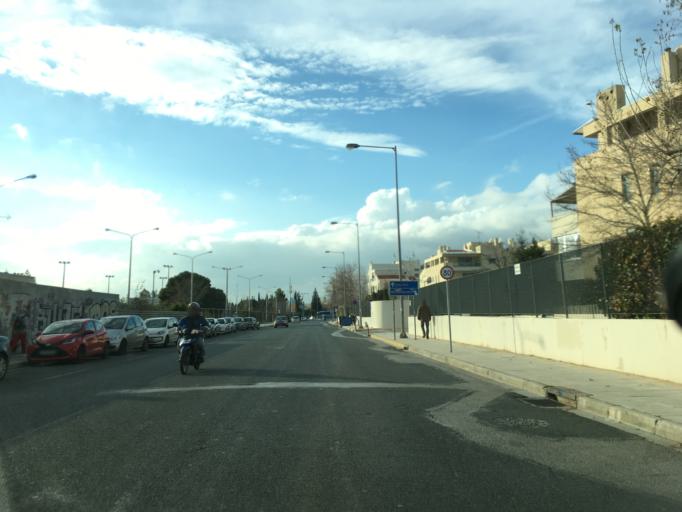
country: GR
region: Attica
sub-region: Nomarchia Athinas
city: Marousi
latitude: 38.0410
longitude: 23.7917
